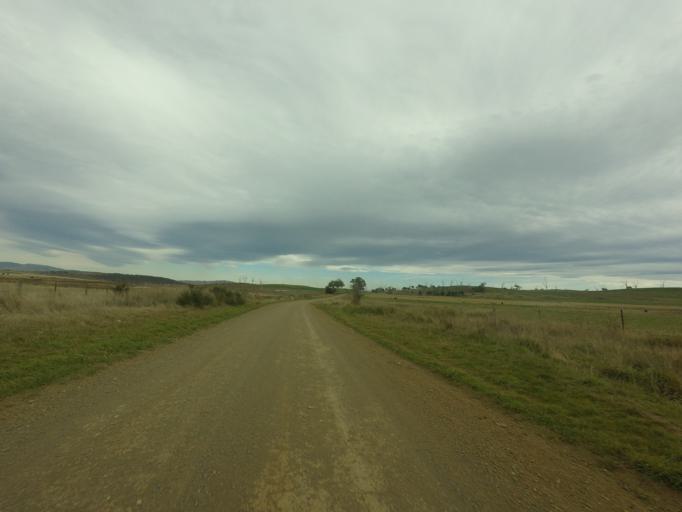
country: AU
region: Tasmania
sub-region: Derwent Valley
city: New Norfolk
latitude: -42.3941
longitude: 146.9735
